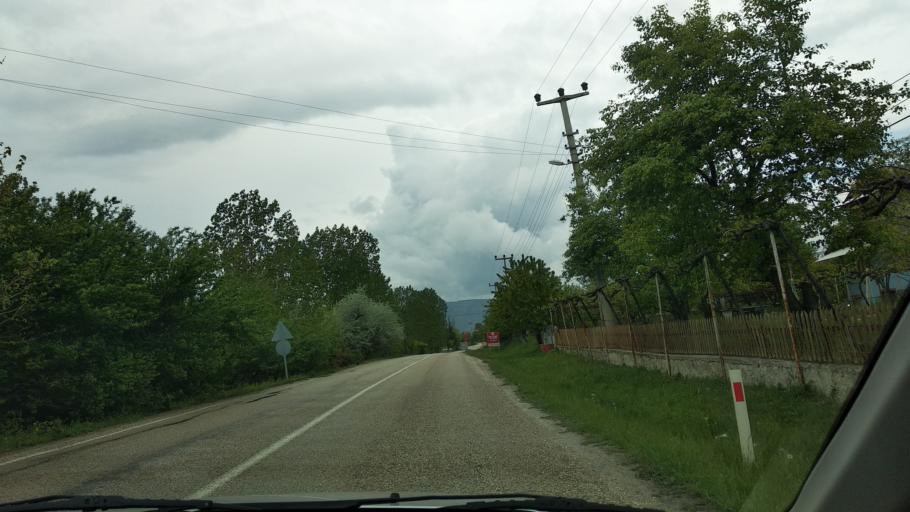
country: TR
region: Bolu
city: Seben
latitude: 40.4169
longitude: 31.5801
